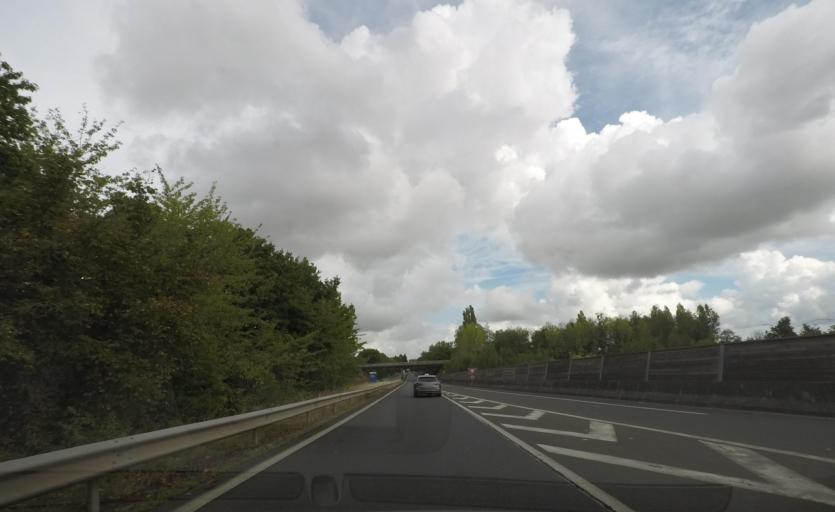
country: FR
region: Pays de la Loire
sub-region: Departement de Maine-et-Loire
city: Pellouailles-les-Vignes
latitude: 47.5201
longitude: -0.4275
